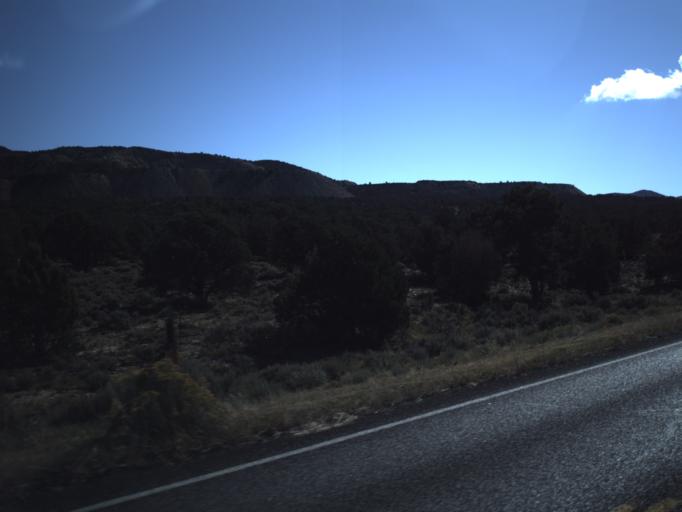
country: US
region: Utah
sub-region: Washington County
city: Enterprise
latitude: 37.6258
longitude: -113.4208
